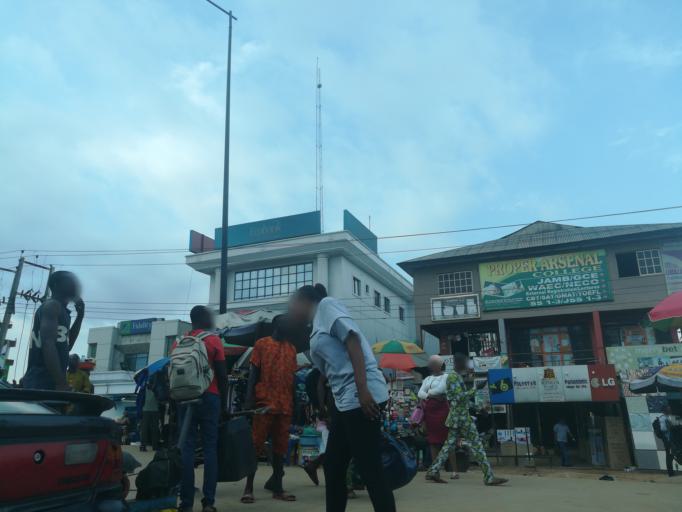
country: NG
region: Lagos
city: Ikorodu
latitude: 6.6223
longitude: 3.4996
